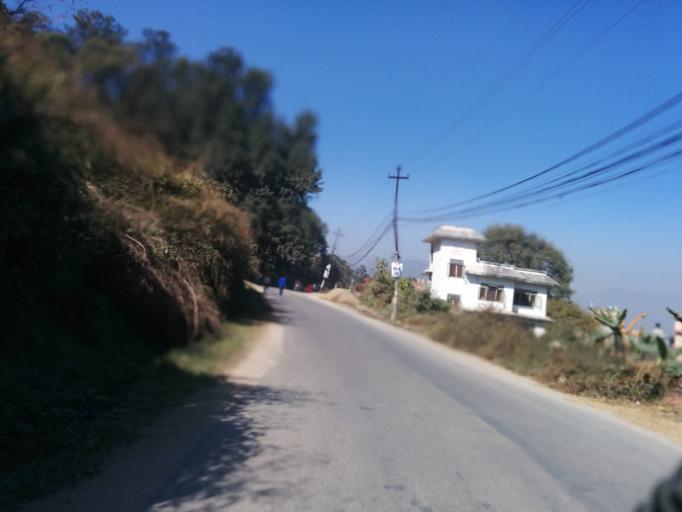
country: NP
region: Central Region
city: Kirtipur
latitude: 27.6801
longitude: 85.2771
